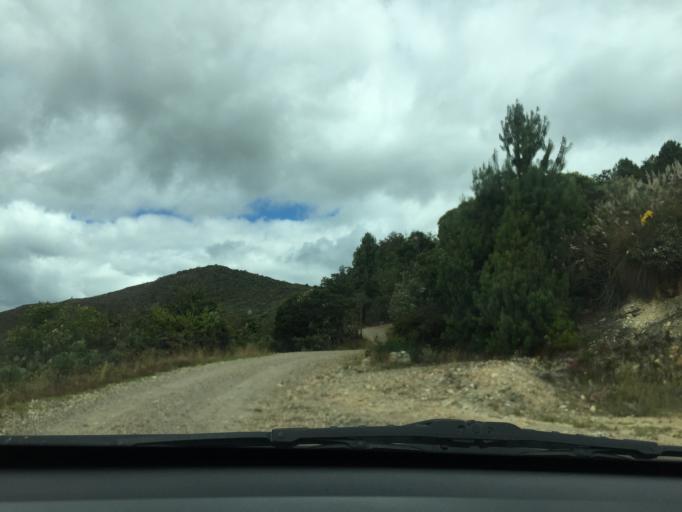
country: CO
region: Cundinamarca
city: Gachancipa
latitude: 4.9613
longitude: -73.8807
